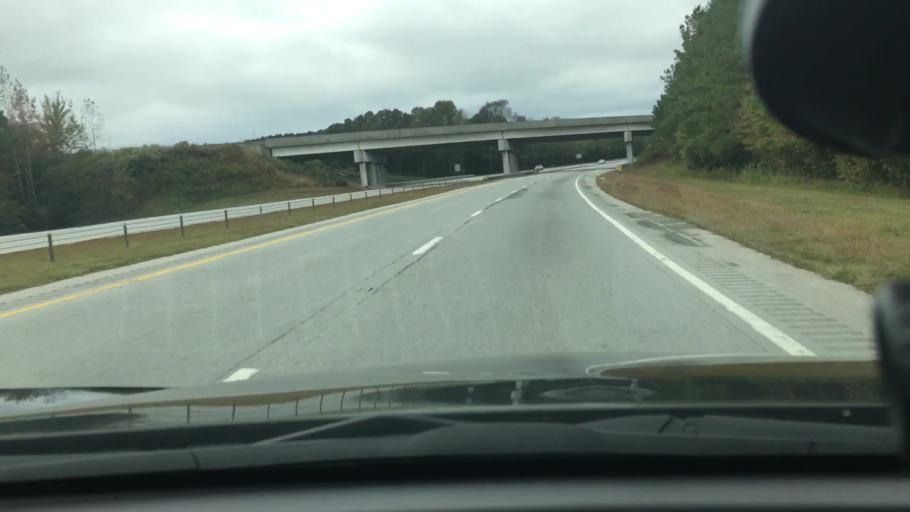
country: US
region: North Carolina
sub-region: Pitt County
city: Farmville
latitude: 35.6147
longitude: -77.6587
